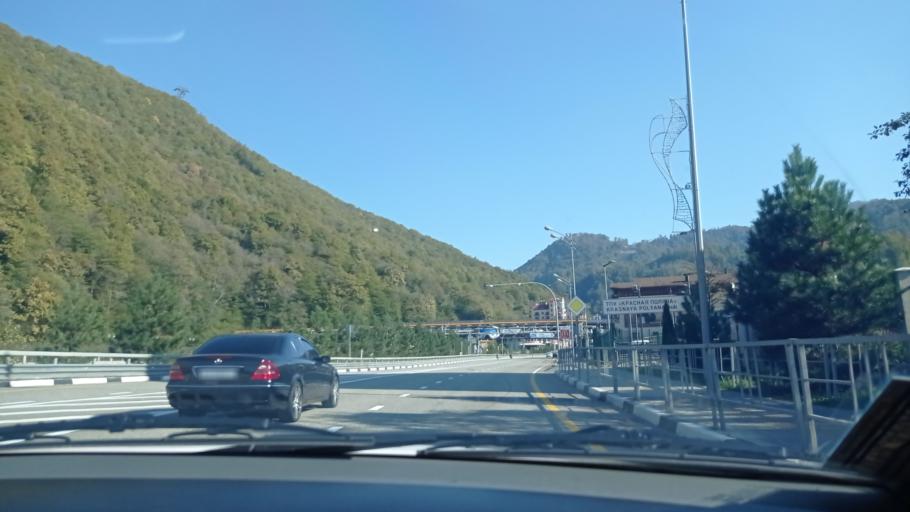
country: RU
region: Krasnodarskiy
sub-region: Sochi City
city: Krasnaya Polyana
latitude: 43.6783
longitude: 40.2806
